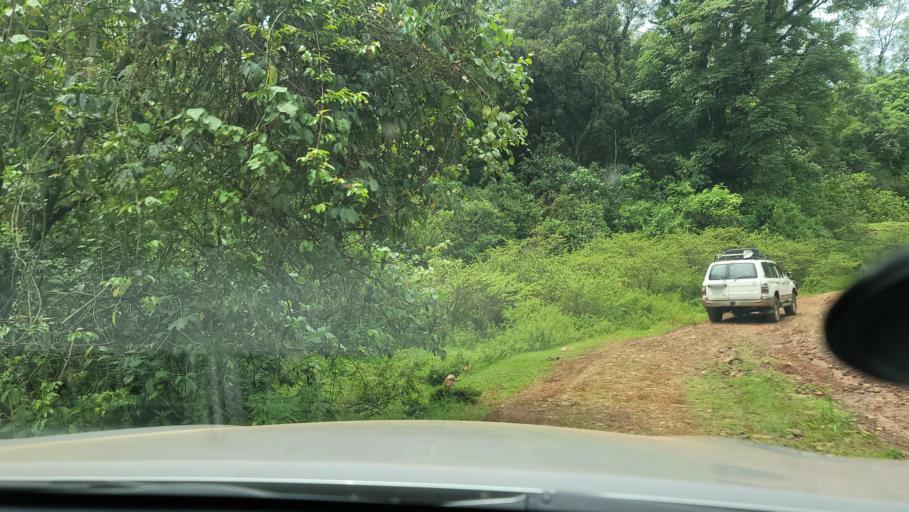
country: ET
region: Southern Nations, Nationalities, and People's Region
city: Bonga
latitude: 7.6826
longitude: 36.2406
